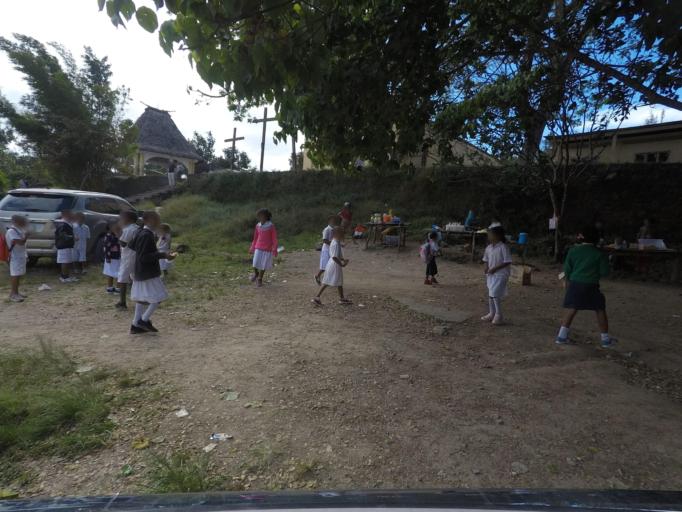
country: TL
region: Baucau
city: Venilale
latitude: -8.6393
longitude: 126.3813
